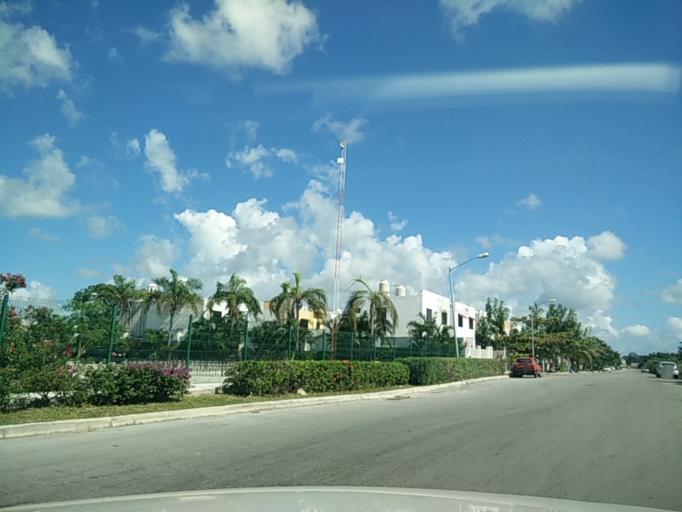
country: MX
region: Quintana Roo
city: Playa del Carmen
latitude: 20.6575
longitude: -87.0651
